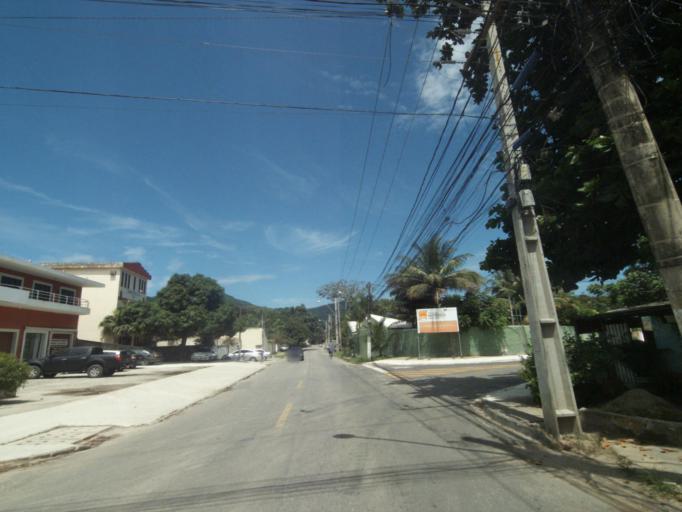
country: BR
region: Rio de Janeiro
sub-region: Niteroi
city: Niteroi
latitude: -22.9268
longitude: -43.0077
